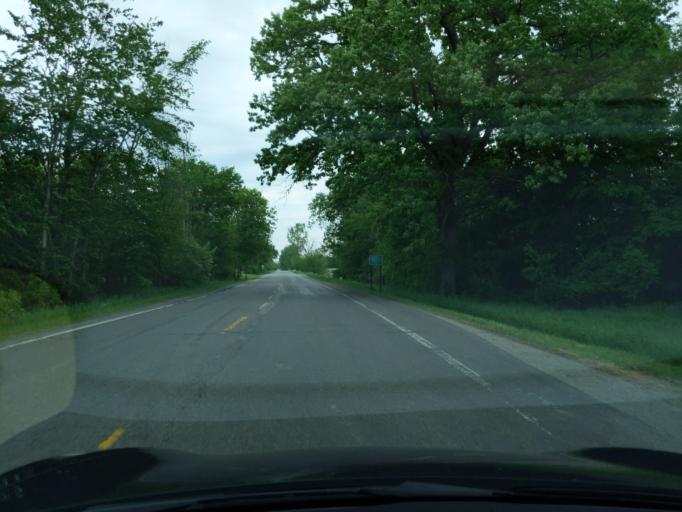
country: US
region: Michigan
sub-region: Ingham County
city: Mason
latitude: 42.6007
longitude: -84.3577
